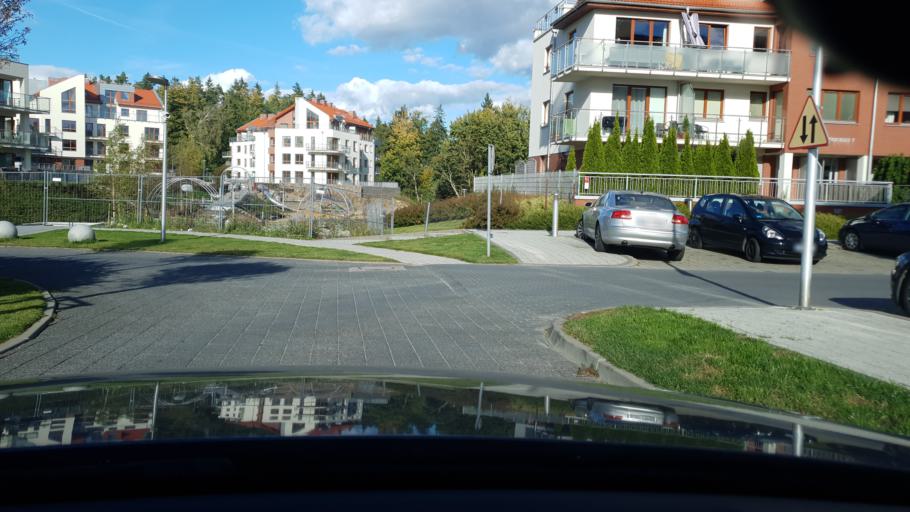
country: PL
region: Pomeranian Voivodeship
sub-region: Powiat kartuski
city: Chwaszczyno
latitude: 54.5011
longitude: 18.4374
